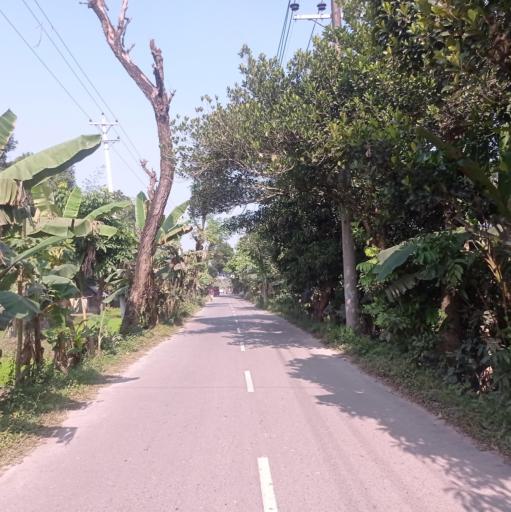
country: BD
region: Dhaka
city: Narsingdi
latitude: 24.0764
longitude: 90.6937
